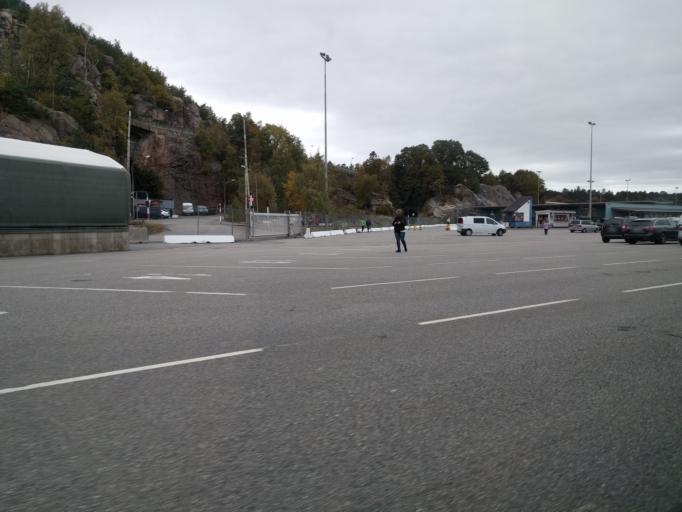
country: NO
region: Vest-Agder
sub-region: Kristiansand
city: Kristiansand
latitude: 58.1418
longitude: 7.9821
